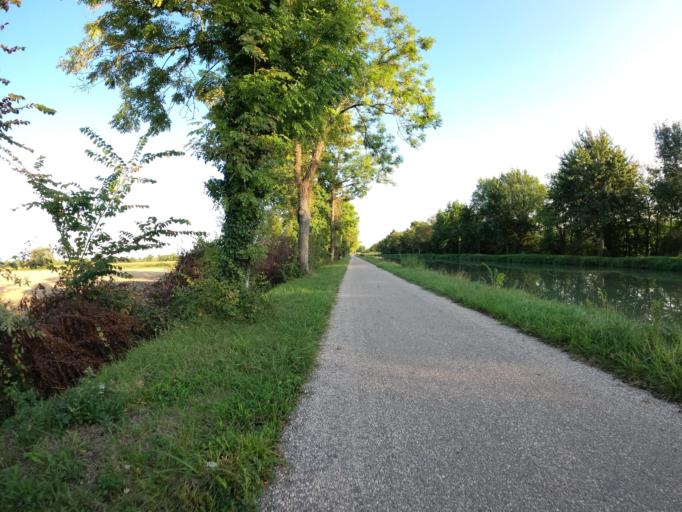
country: FR
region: Midi-Pyrenees
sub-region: Departement du Tarn-et-Garonne
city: Saint-Porquier
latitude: 44.0199
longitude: 1.1675
